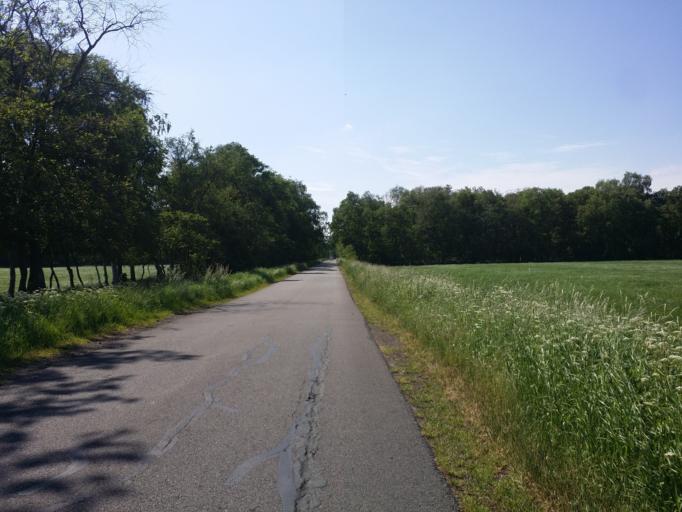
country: DE
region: Lower Saxony
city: Elsfleth
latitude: 53.2049
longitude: 8.3390
